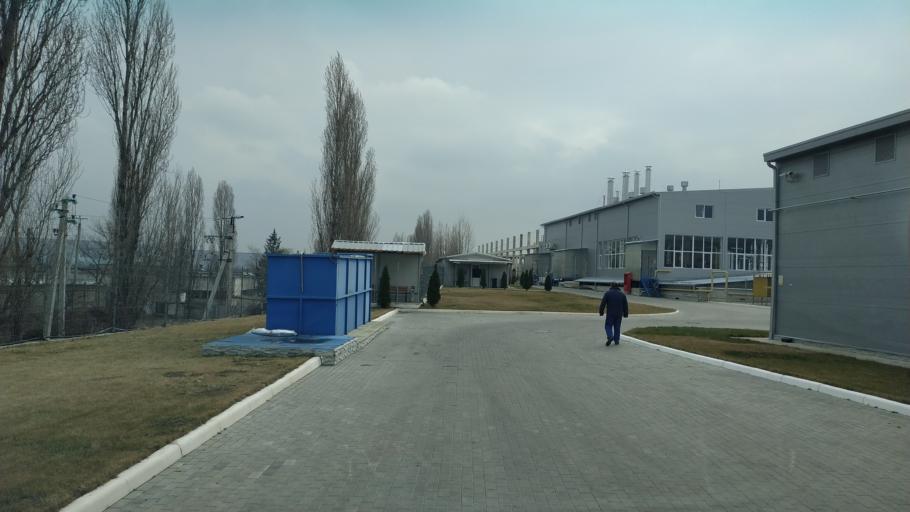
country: MD
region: Chisinau
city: Singera
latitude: 46.9086
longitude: 29.0089
